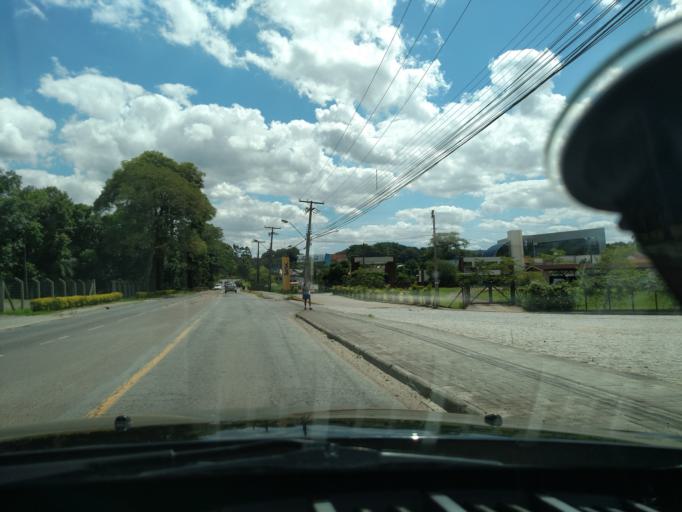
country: BR
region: Santa Catarina
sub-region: Blumenau
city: Blumenau
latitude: -26.8728
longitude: -49.1013
